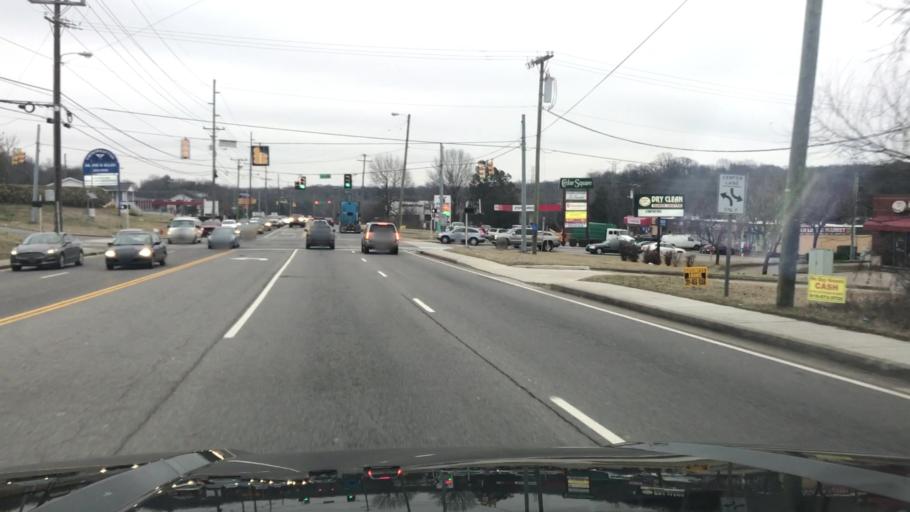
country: US
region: Tennessee
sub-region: Williamson County
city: Brentwood Estates
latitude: 36.0455
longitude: -86.7045
